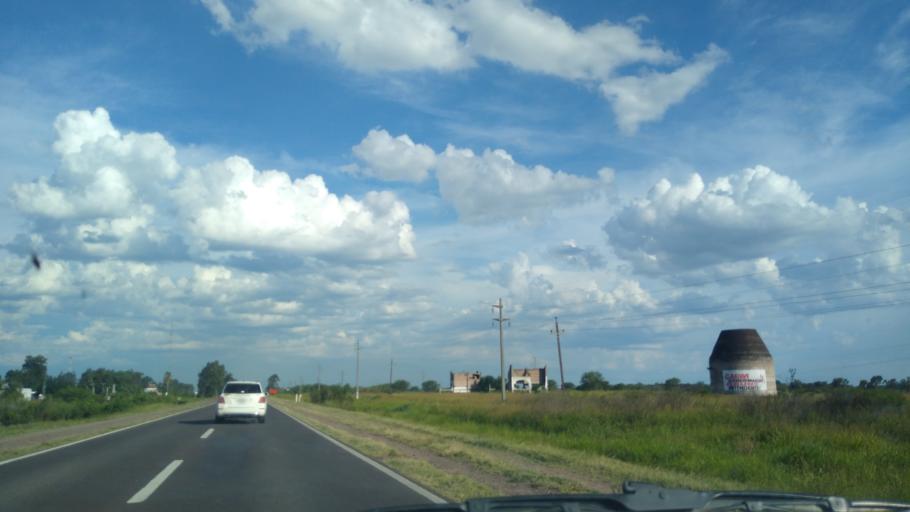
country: AR
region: Chaco
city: Presidencia Roque Saenz Pena
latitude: -26.8219
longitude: -60.3917
